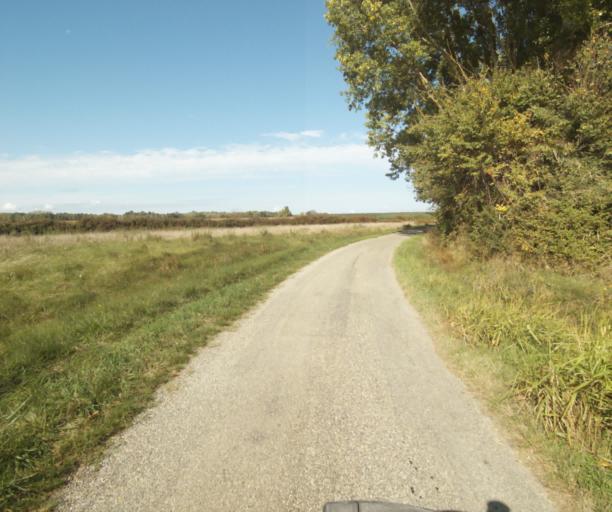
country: FR
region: Midi-Pyrenees
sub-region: Departement du Tarn-et-Garonne
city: Finhan
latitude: 43.8946
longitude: 1.2207
